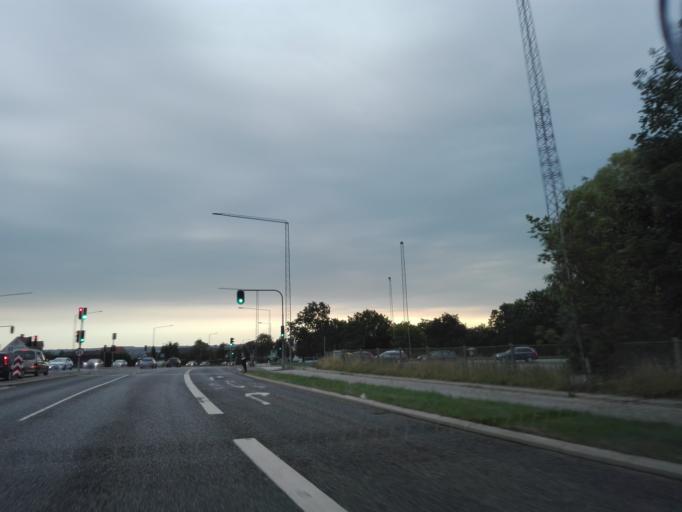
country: DK
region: Central Jutland
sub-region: Arhus Kommune
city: Arhus
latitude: 56.1949
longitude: 10.2198
